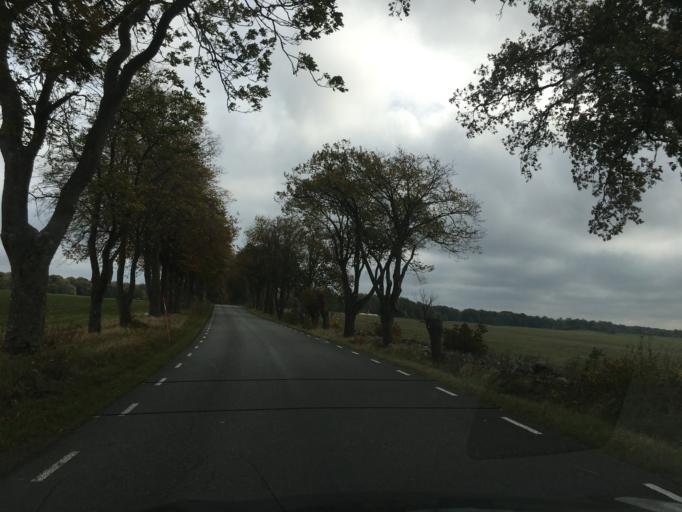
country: SE
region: Skane
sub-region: Tomelilla Kommun
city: Tomelilla
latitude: 55.6481
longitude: 14.0369
